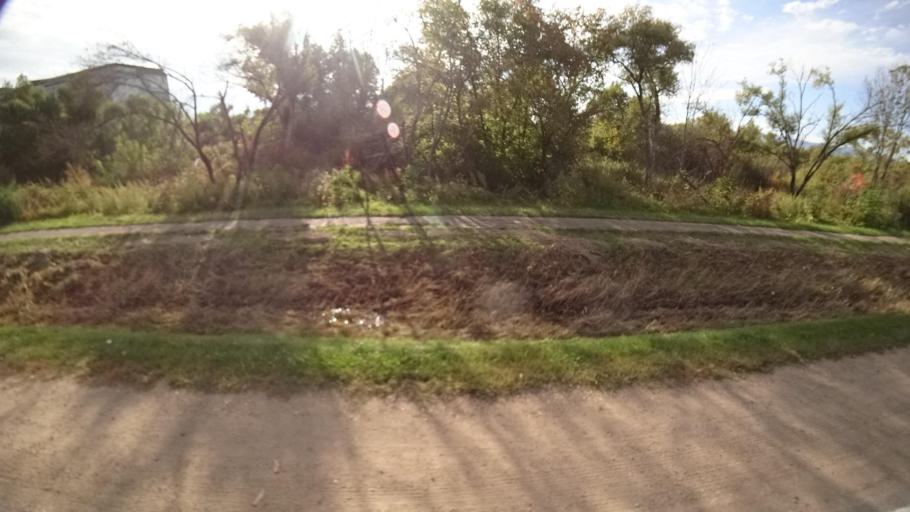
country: RU
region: Primorskiy
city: Dostoyevka
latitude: 44.2926
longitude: 133.4264
